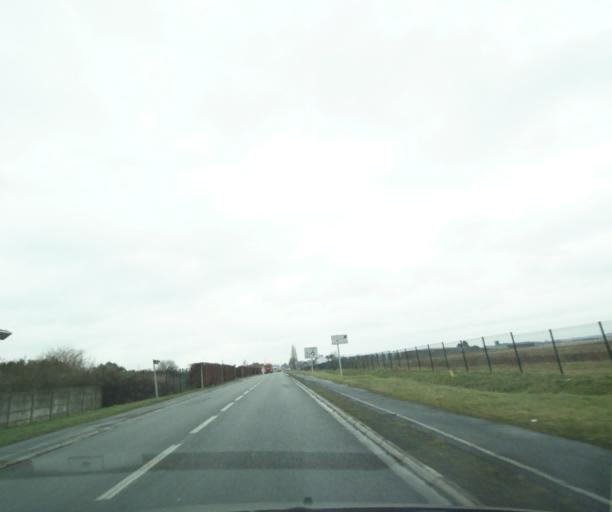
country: FR
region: Nord-Pas-de-Calais
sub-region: Departement du Nord
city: Prouvy
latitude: 50.3295
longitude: 3.4464
